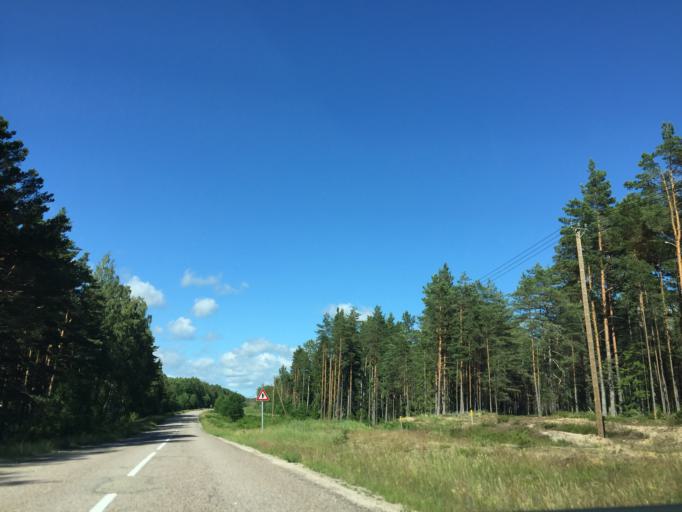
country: LV
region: Ventspils
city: Ventspils
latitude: 57.4831
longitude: 21.6722
